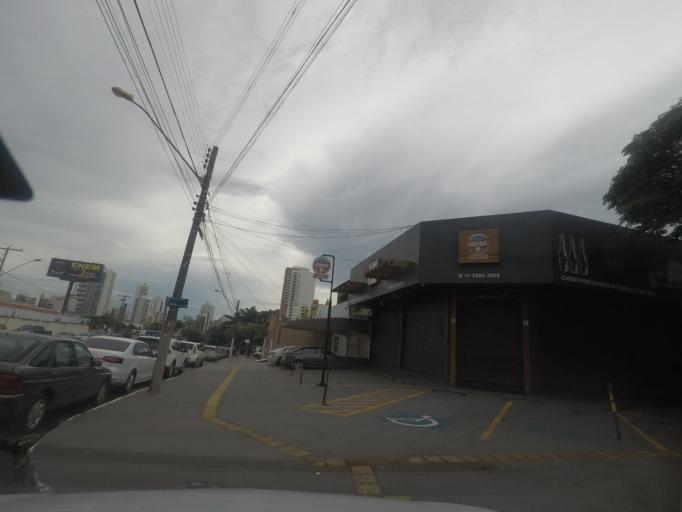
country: BR
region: Goias
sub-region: Goiania
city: Goiania
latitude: -16.6953
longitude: -49.2694
